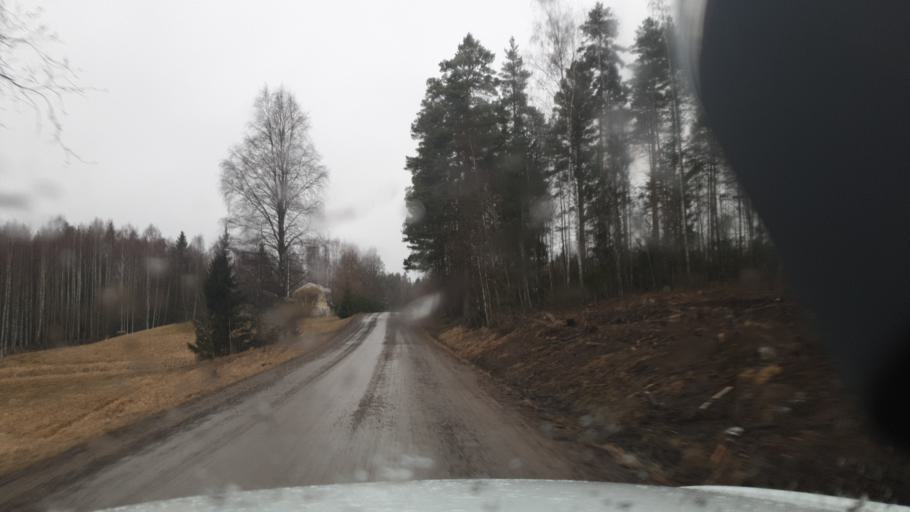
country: SE
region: Vaermland
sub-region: Eda Kommun
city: Amotfors
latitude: 59.7771
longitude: 12.3419
